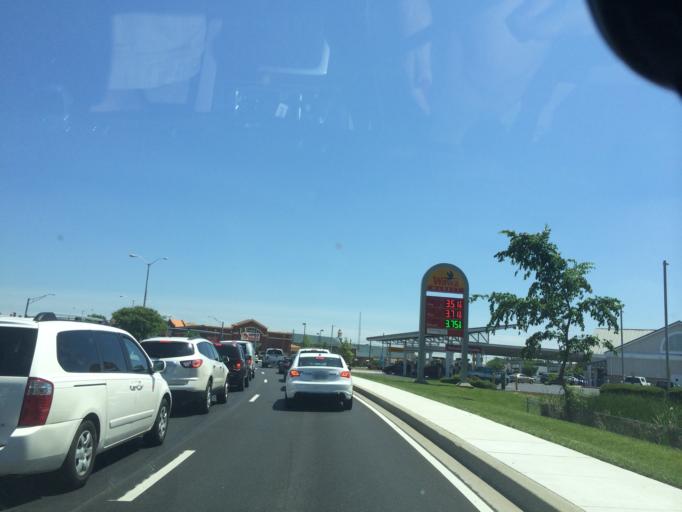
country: US
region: Maryland
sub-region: Dorchester County
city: Cambridge
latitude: 38.5619
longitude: -76.0659
